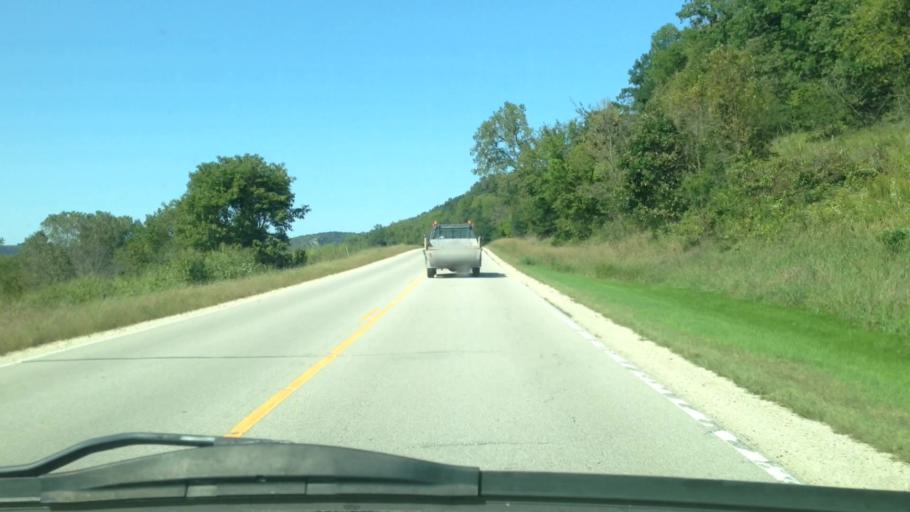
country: US
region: Minnesota
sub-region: Fillmore County
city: Rushford
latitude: 43.7734
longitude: -91.7634
